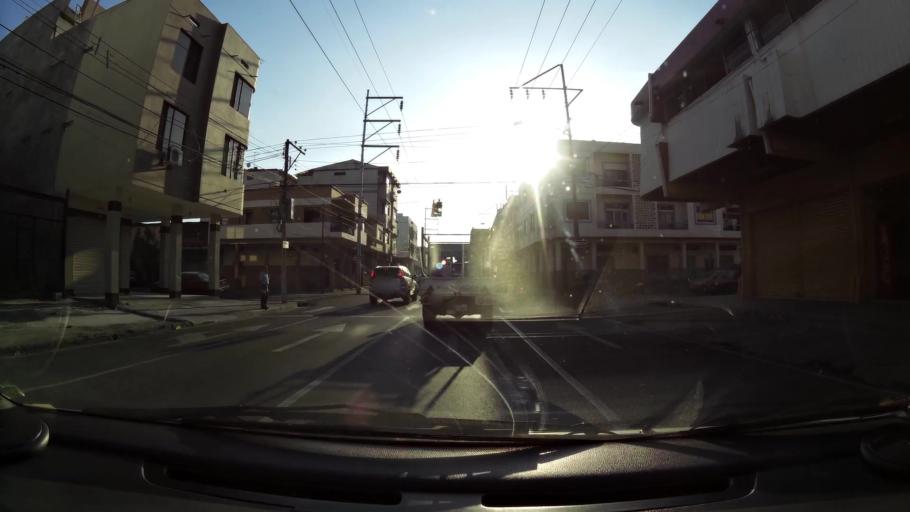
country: EC
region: Guayas
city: Guayaquil
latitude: -2.2095
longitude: -79.8886
